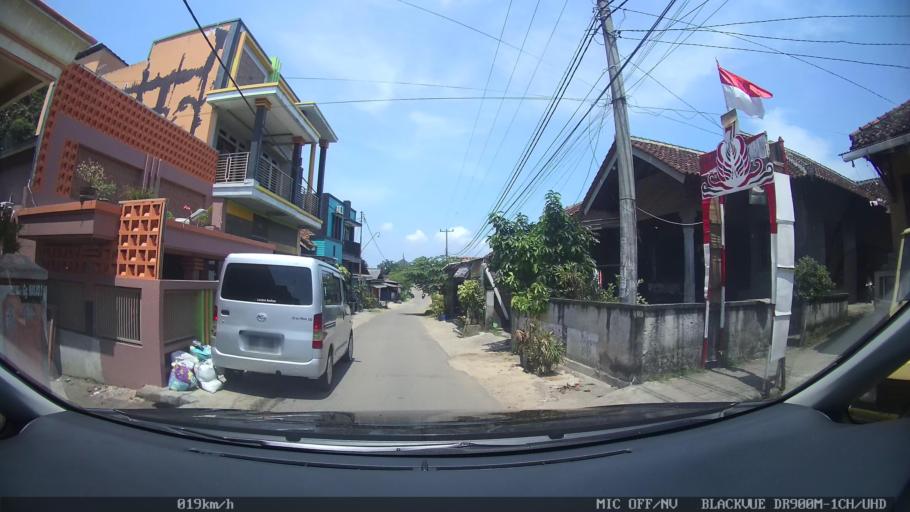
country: ID
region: Lampung
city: Kedaton
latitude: -5.3915
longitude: 105.2677
